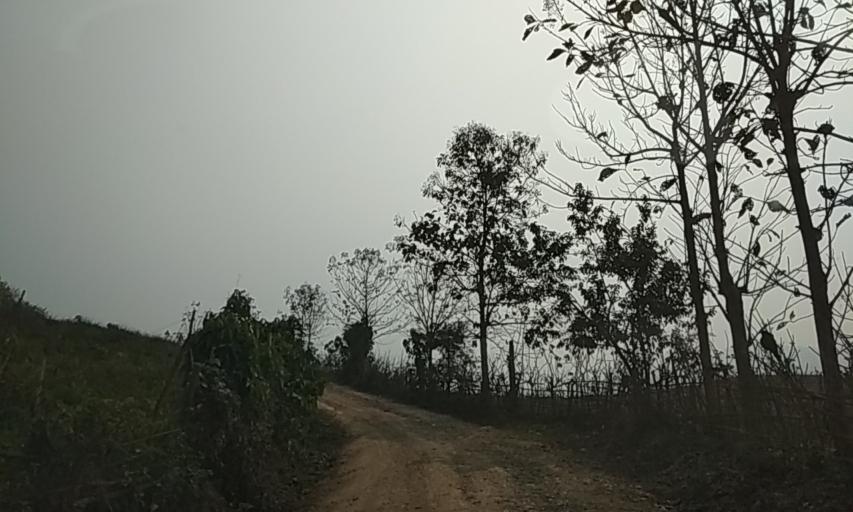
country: TH
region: Nan
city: Chaloem Phra Kiat
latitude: 19.9256
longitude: 101.1614
